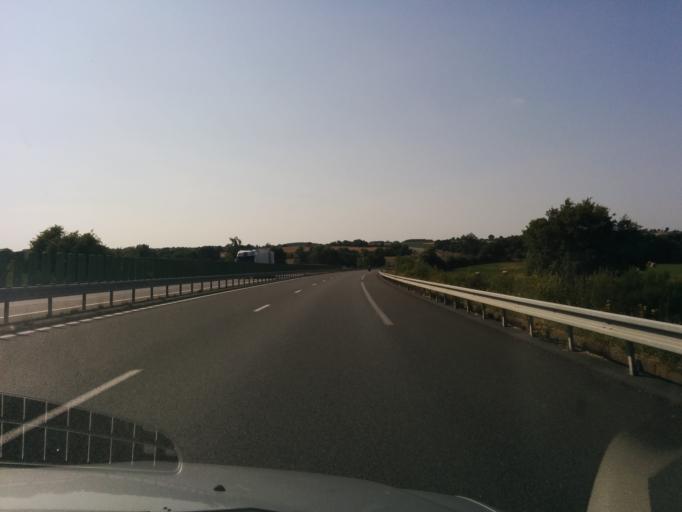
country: FR
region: Poitou-Charentes
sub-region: Departement des Deux-Sevres
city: Combrand
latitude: 46.9076
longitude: -0.6774
